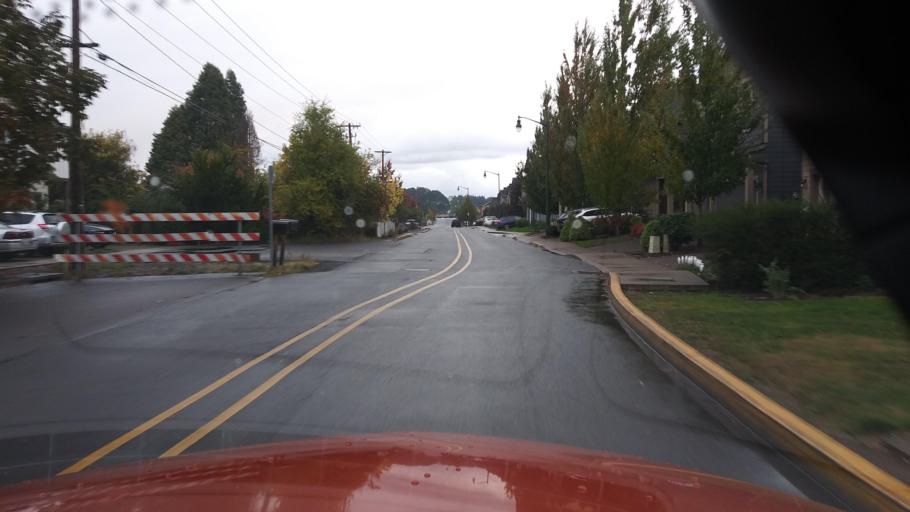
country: US
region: Oregon
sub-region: Washington County
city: Forest Grove
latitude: 45.5274
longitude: -123.0984
